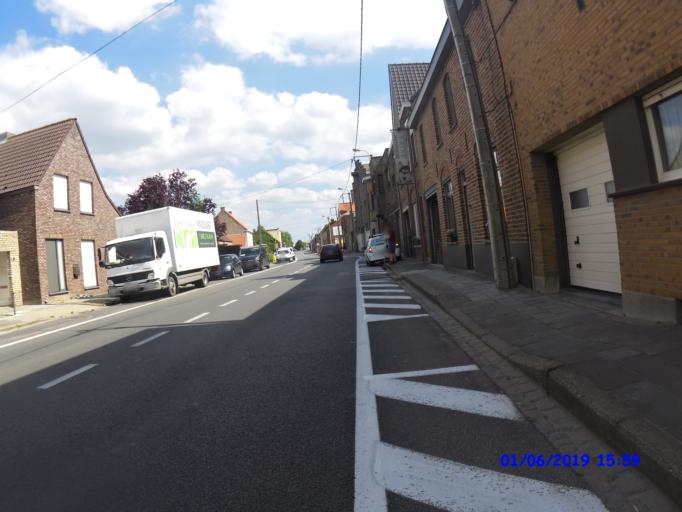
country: BE
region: Flanders
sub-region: Provincie West-Vlaanderen
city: Diksmuide
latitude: 51.0272
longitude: 2.9052
